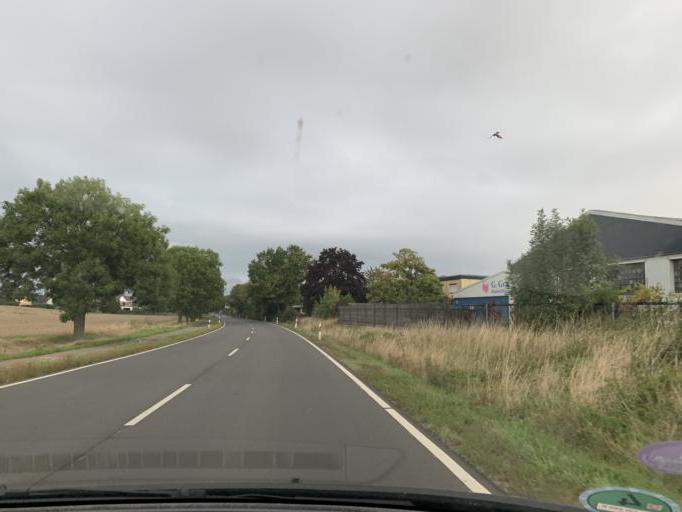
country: DE
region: North Rhine-Westphalia
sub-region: Regierungsbezirk Koln
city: Dueren
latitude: 50.8247
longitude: 6.4418
